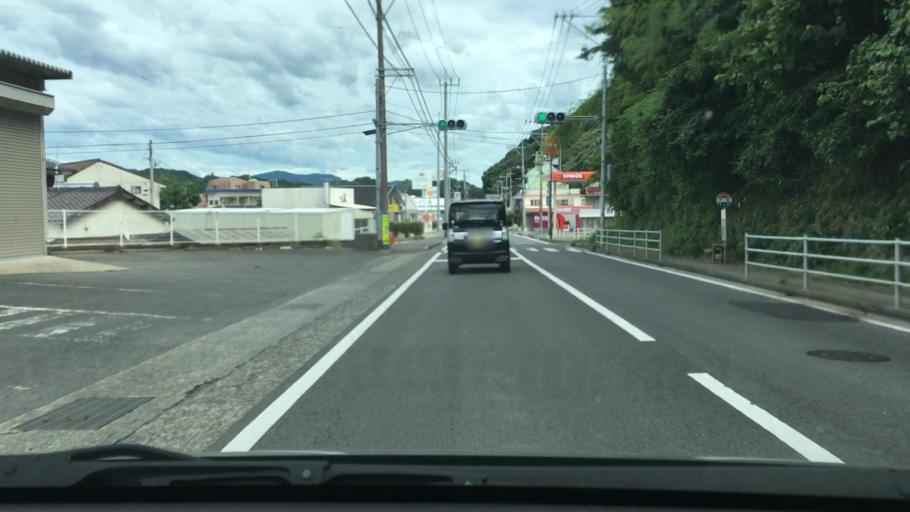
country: JP
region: Nagasaki
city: Togitsu
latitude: 32.8894
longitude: 129.7853
